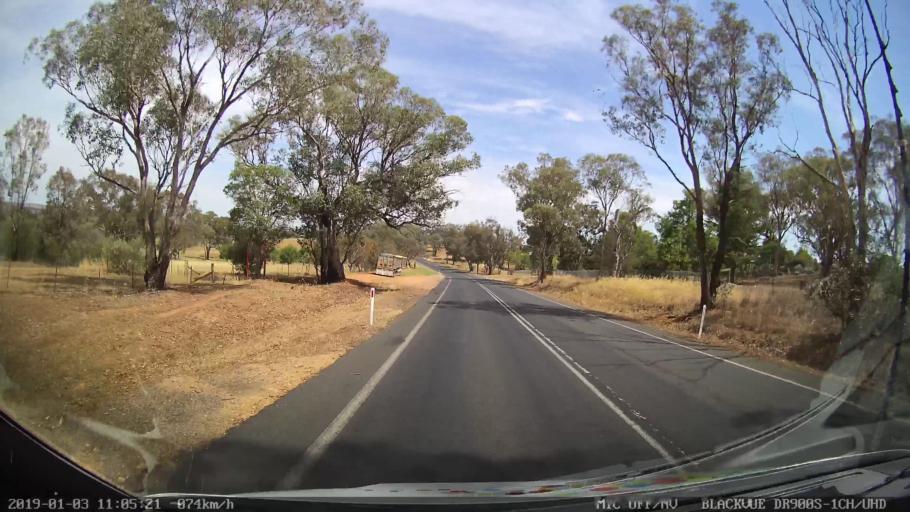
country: AU
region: New South Wales
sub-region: Young
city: Young
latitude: -34.2729
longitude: 148.2856
